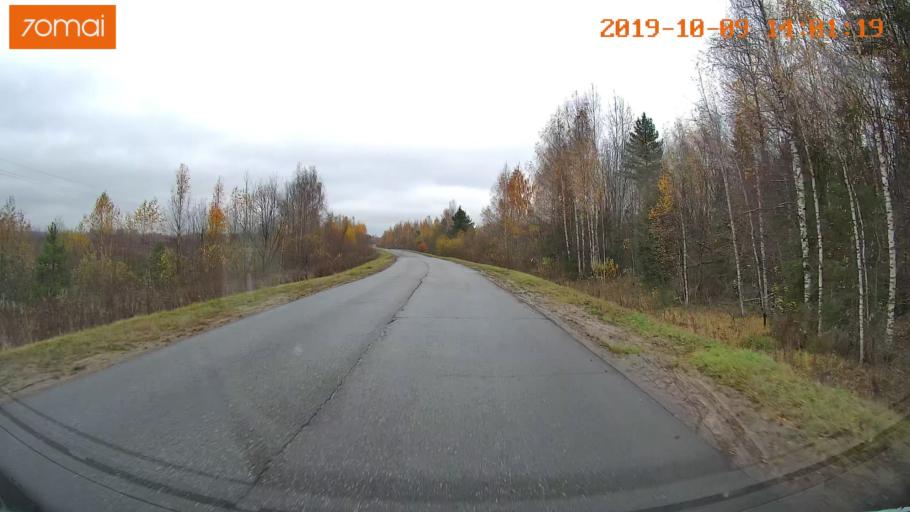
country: RU
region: Kostroma
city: Buy
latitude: 58.4427
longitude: 41.3462
